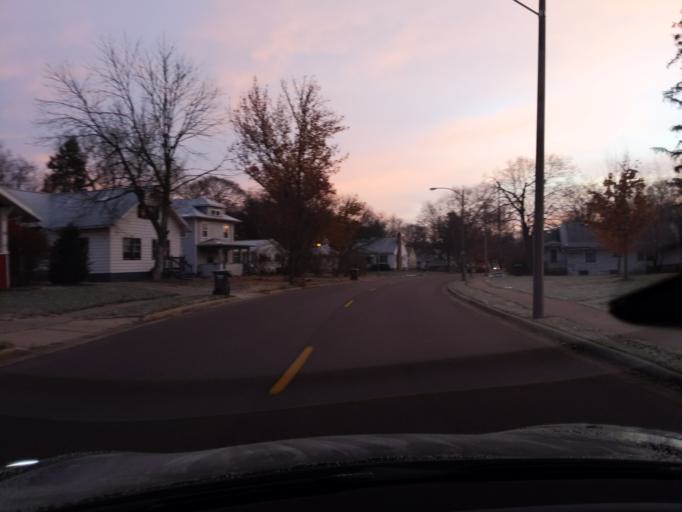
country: US
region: Michigan
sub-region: Ingham County
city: Lansing
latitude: 42.7050
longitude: -84.5543
